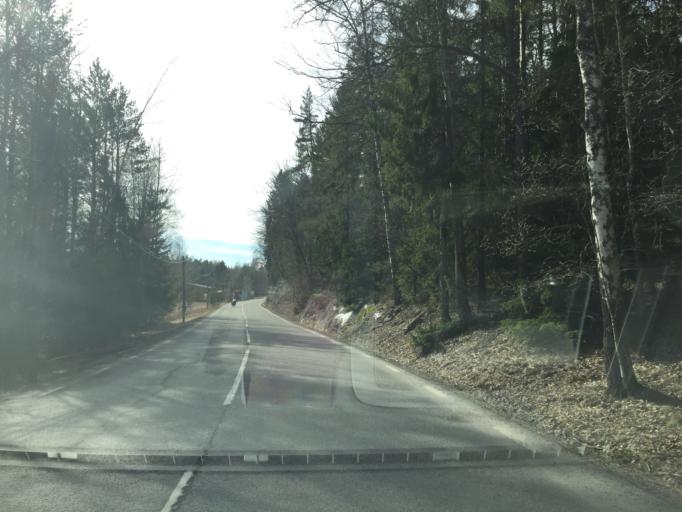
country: SE
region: Stockholm
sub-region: Huddinge Kommun
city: Huddinge
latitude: 59.1099
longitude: 17.9912
